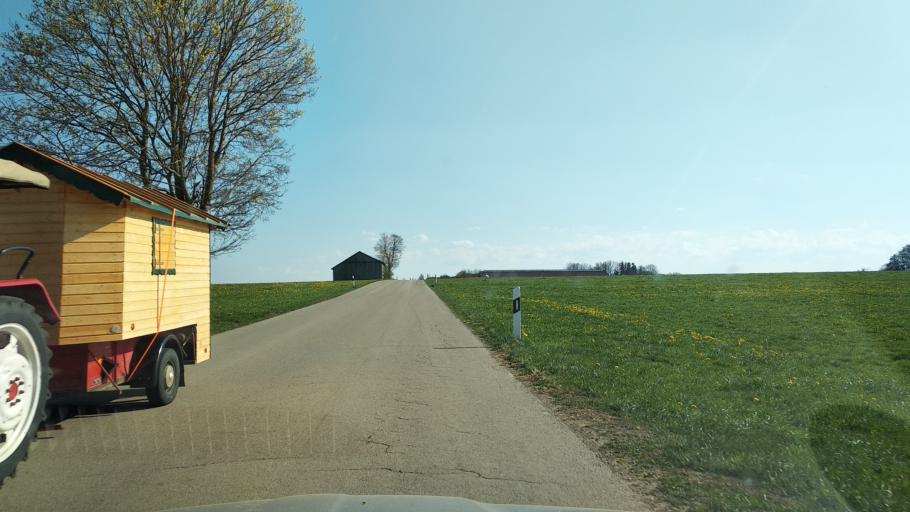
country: DE
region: Bavaria
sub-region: Swabia
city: Wald
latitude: 47.9851
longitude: 10.3099
